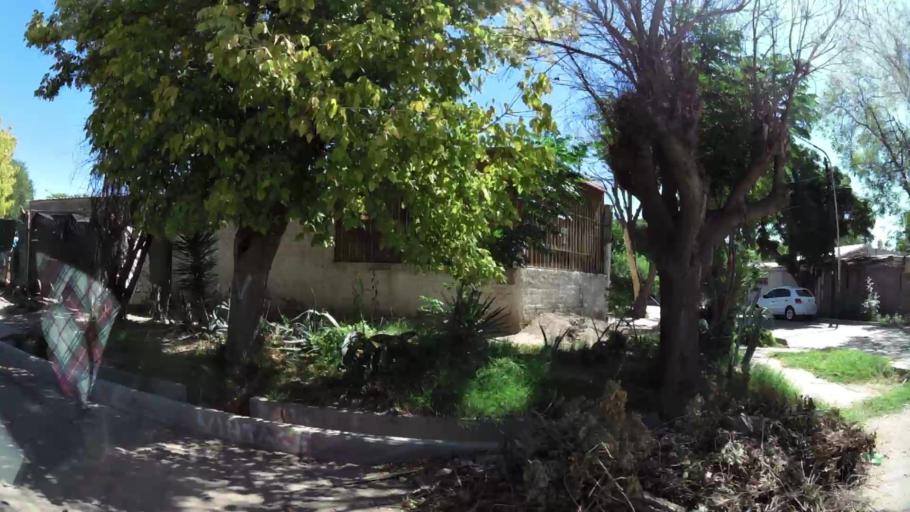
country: AR
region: Mendoza
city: Las Heras
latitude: -32.8330
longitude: -68.8360
